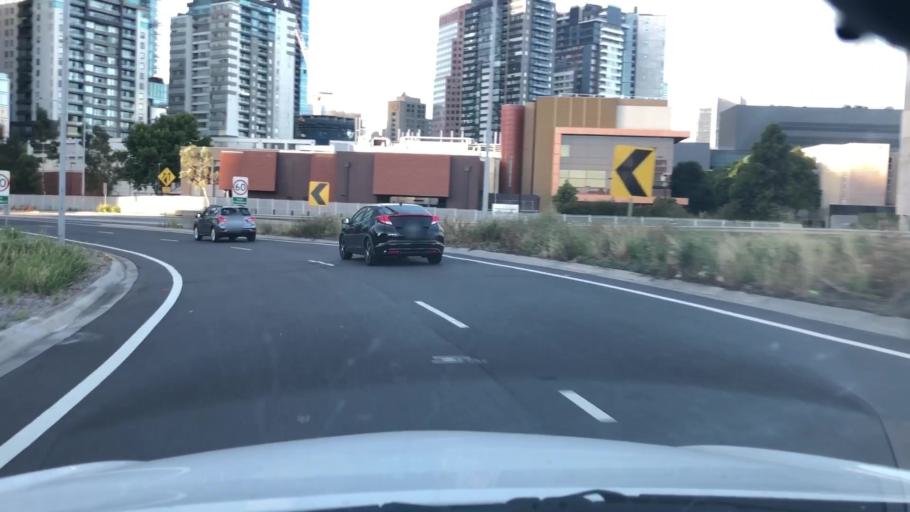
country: AU
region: Victoria
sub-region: Melbourne
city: Southbank
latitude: -37.8259
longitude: 144.9648
